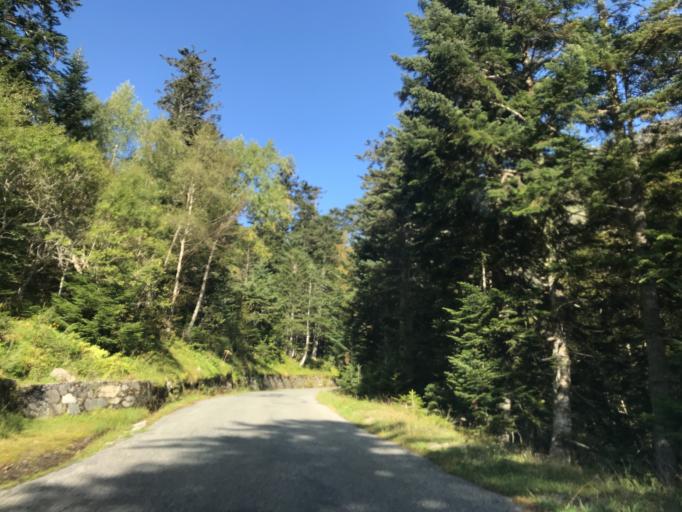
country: FR
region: Midi-Pyrenees
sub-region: Departement des Hautes-Pyrenees
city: Saint-Lary-Soulan
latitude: 42.8149
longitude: 0.2008
